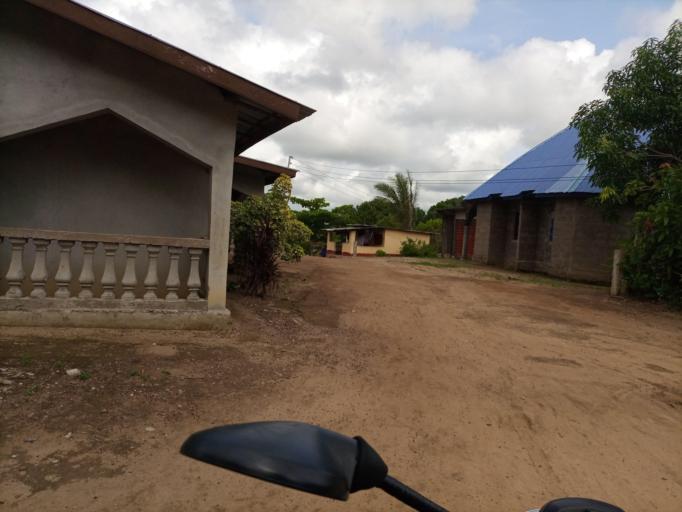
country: SL
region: Southern Province
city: Bo
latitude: 7.9693
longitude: -11.7649
